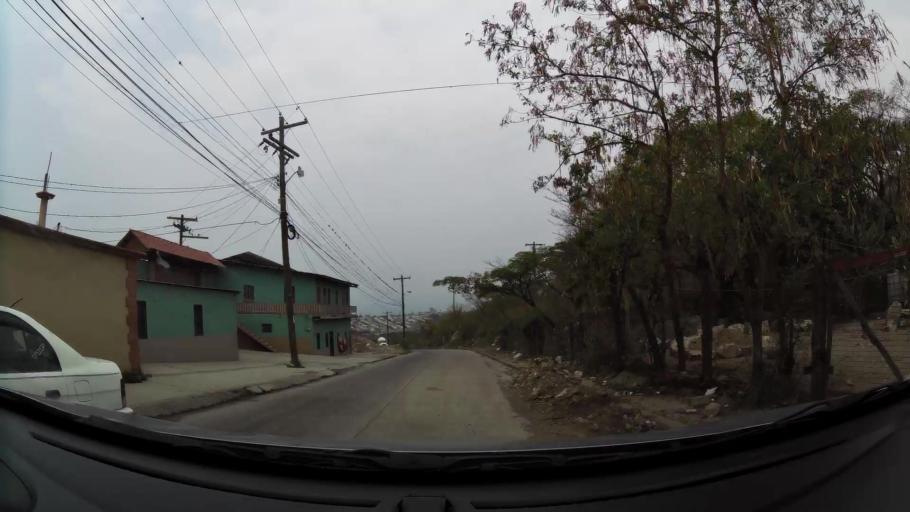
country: HN
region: Francisco Morazan
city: Tegucigalpa
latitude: 14.0692
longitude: -87.2427
